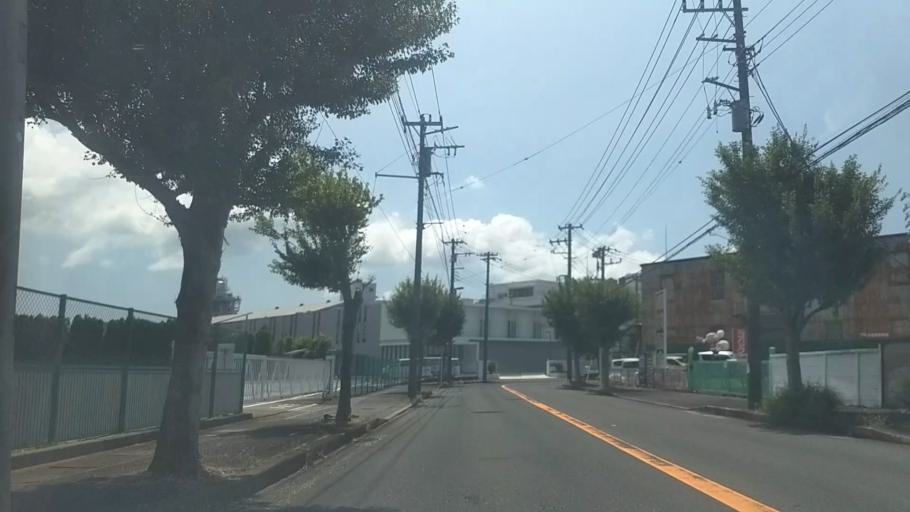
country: JP
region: Kanagawa
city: Yokosuka
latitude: 35.3128
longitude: 139.6415
